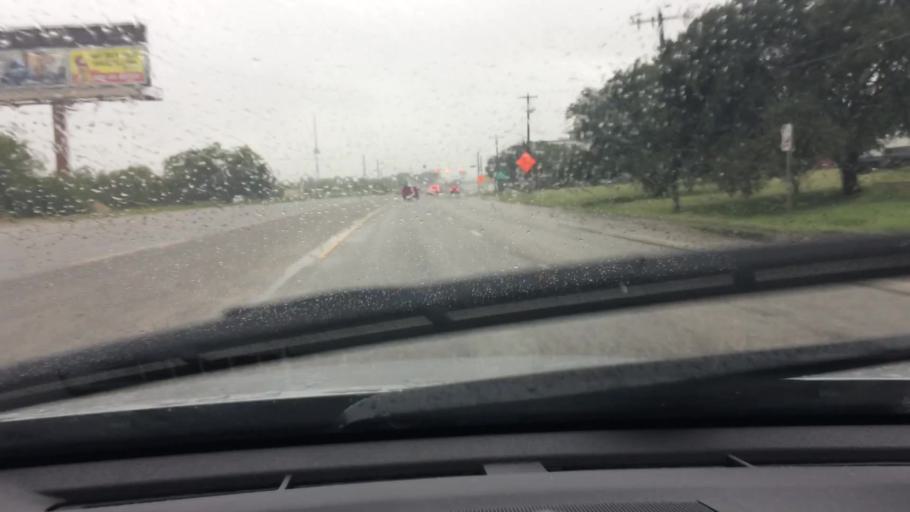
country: US
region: Texas
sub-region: Bexar County
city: Kirby
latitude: 29.4755
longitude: -98.3730
